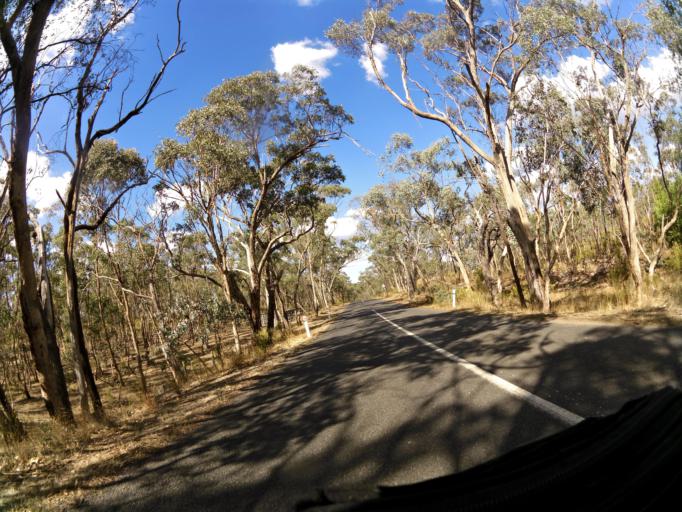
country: AU
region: Victoria
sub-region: Greater Bendigo
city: Kennington
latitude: -36.9534
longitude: 144.7672
